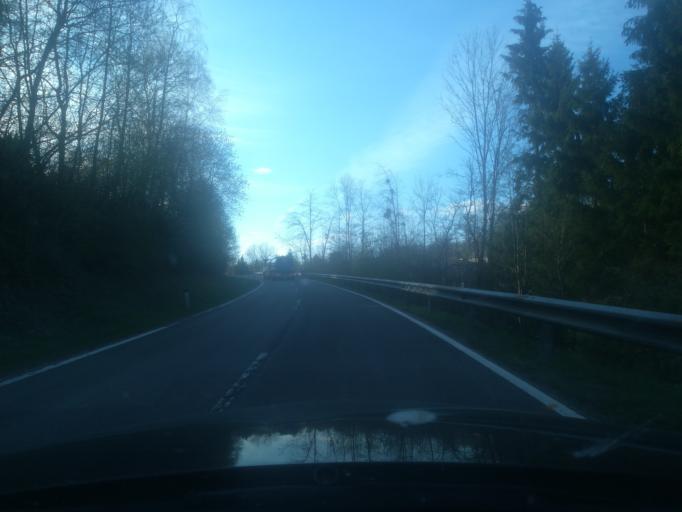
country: AT
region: Upper Austria
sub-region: Politischer Bezirk Perg
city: Bad Kreuzen
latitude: 48.2595
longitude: 14.8140
